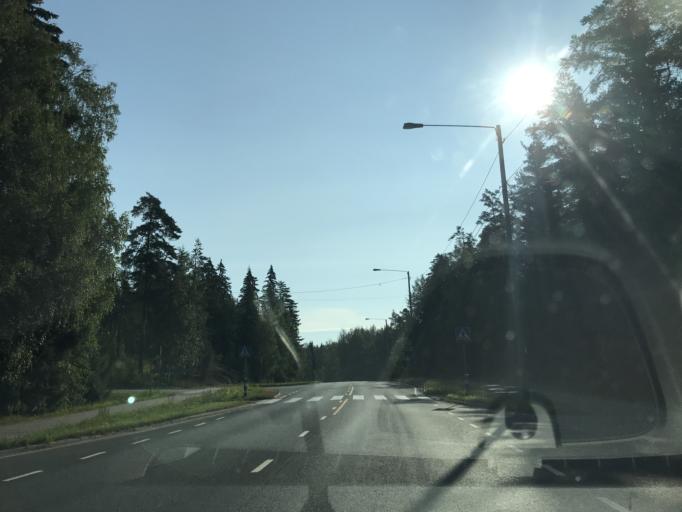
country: FI
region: Paijanne Tavastia
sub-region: Lahti
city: Orimattila
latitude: 60.7958
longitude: 25.7182
